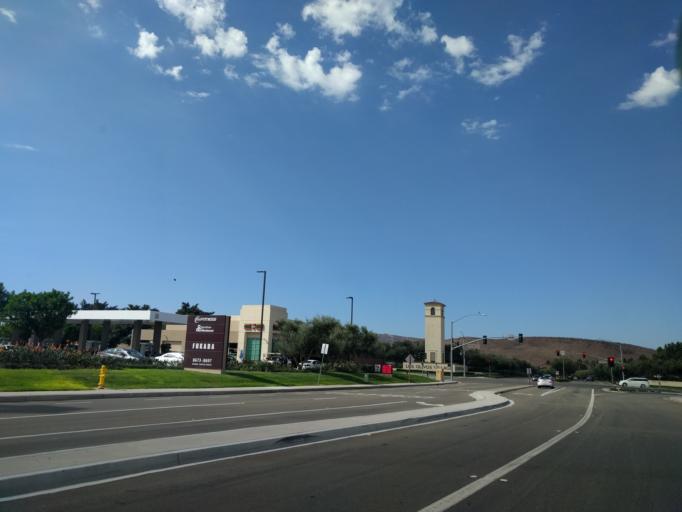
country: US
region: California
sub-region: Orange County
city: Laguna Woods
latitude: 33.6448
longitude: -117.7437
